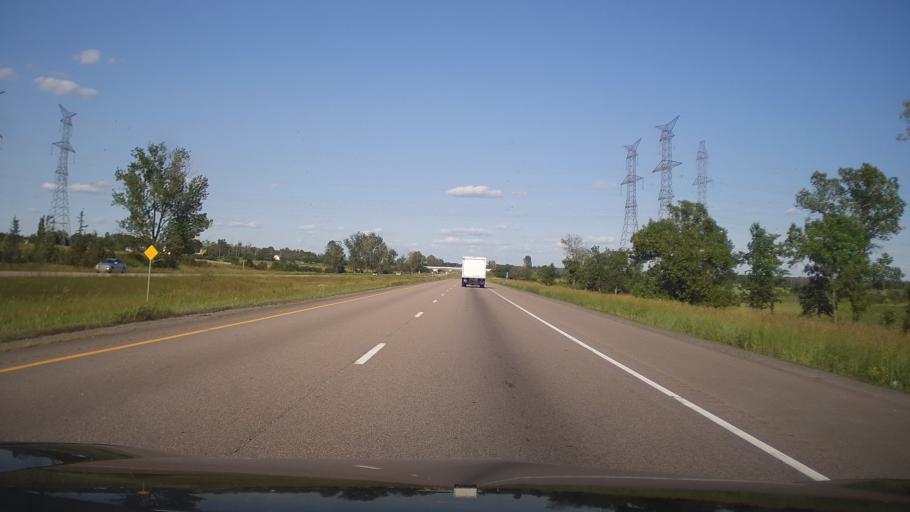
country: CA
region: Ontario
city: Deseronto
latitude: 44.2509
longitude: -77.0157
